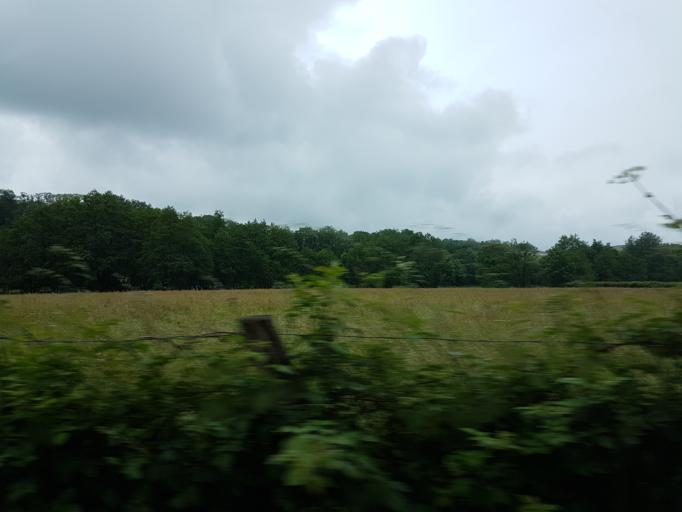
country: FR
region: Bourgogne
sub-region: Departement de la Nievre
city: Lormes
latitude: 47.1830
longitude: 3.7927
